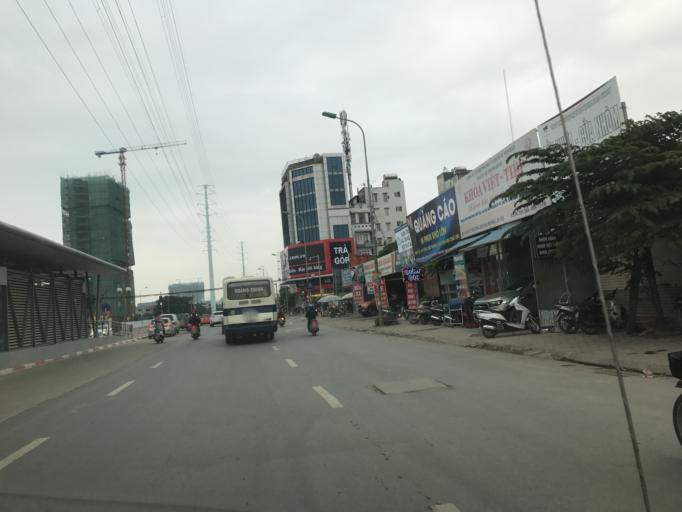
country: VN
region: Ha Noi
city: Ha Dong
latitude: 20.9822
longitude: 105.7699
